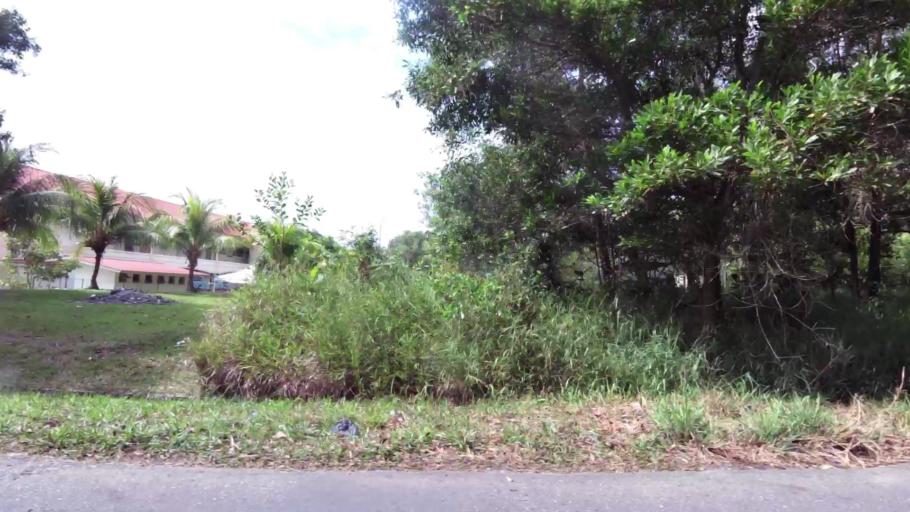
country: BN
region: Brunei and Muara
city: Bandar Seri Begawan
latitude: 4.9360
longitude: 114.9062
